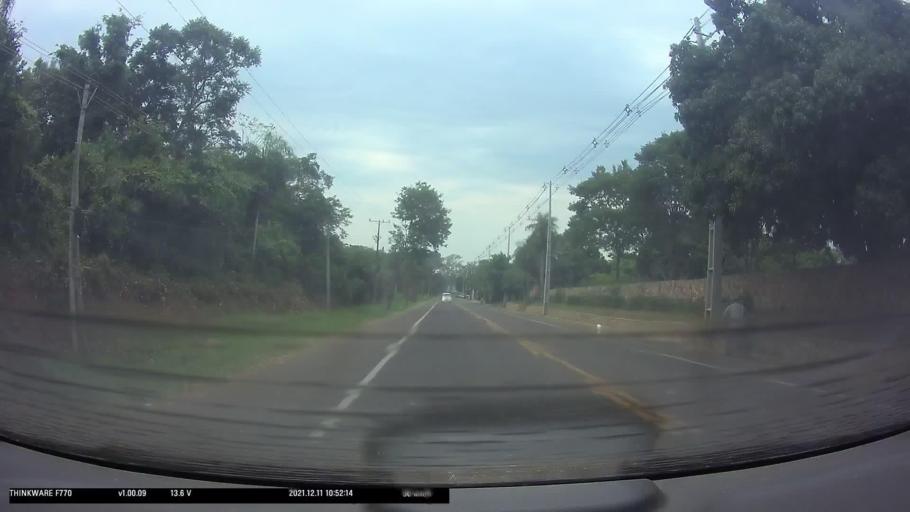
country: PY
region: Cordillera
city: San Bernardino
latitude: -25.2937
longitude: -57.2689
